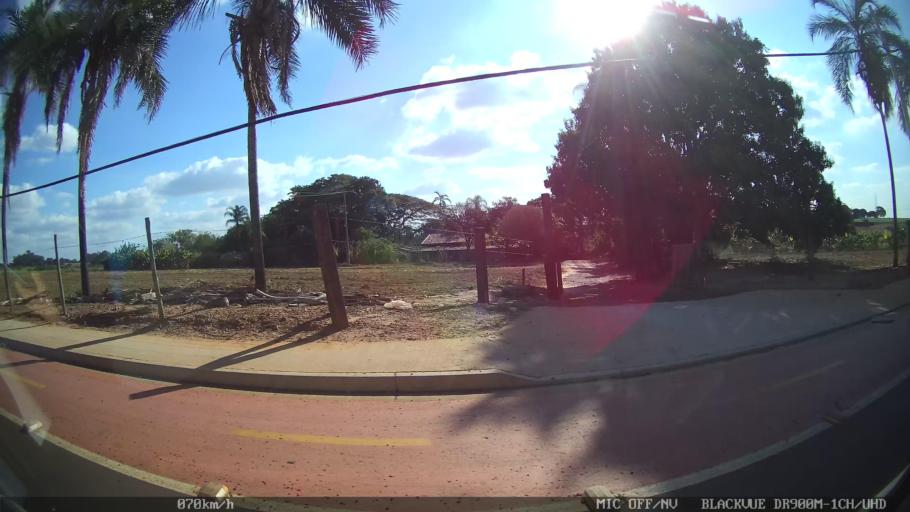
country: BR
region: Sao Paulo
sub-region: Nova Odessa
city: Nova Odessa
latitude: -22.8048
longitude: -47.3186
